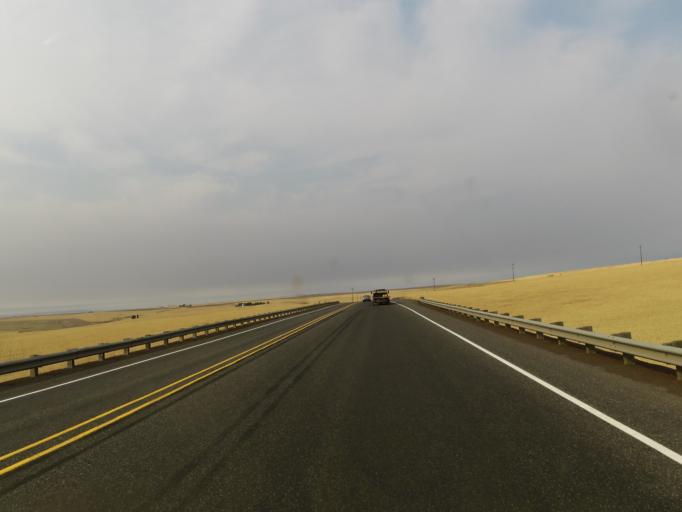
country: US
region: Oregon
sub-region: Sherman County
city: Moro
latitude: 45.4191
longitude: -120.7755
